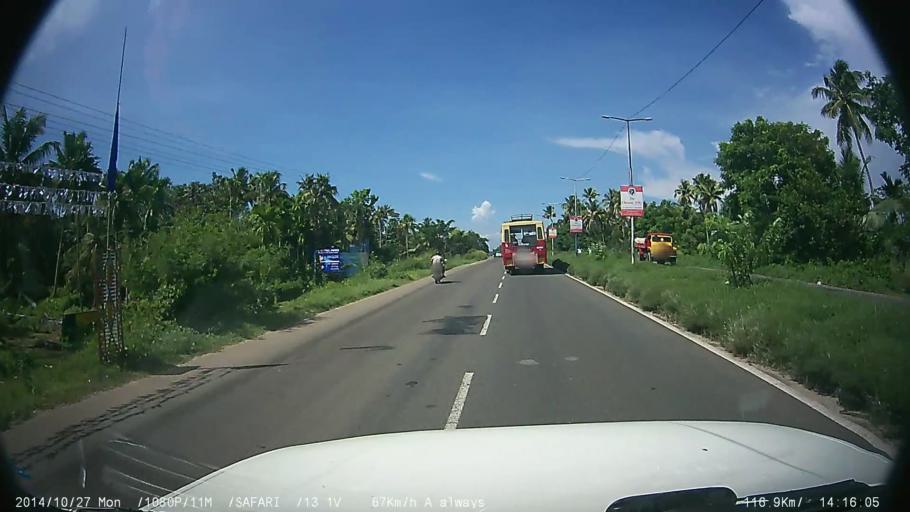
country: IN
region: Kerala
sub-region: Alappuzha
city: Kutiatodu
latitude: 9.8391
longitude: 76.3091
